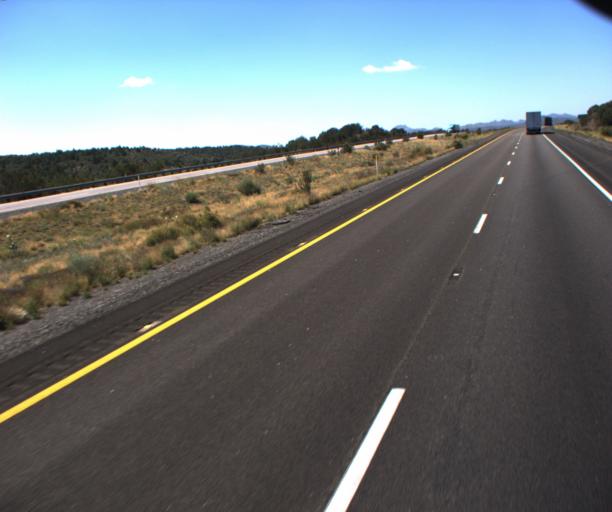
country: US
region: Arizona
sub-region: Mohave County
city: Peach Springs
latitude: 35.1963
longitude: -113.3072
